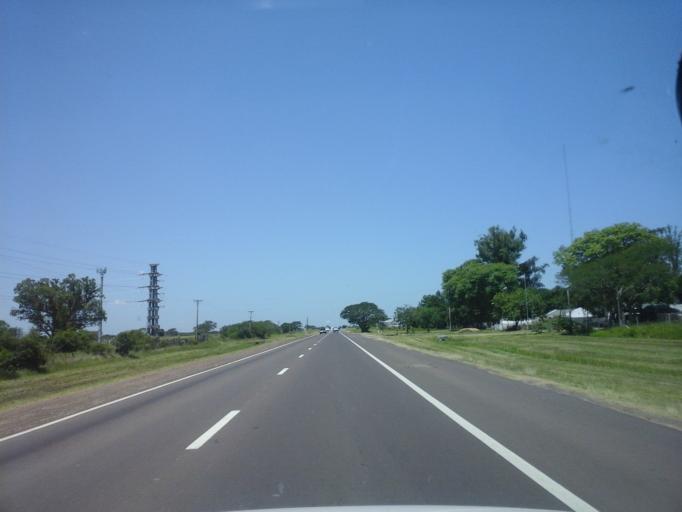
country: AR
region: Corrientes
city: Corrientes
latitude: -27.4260
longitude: -58.7142
